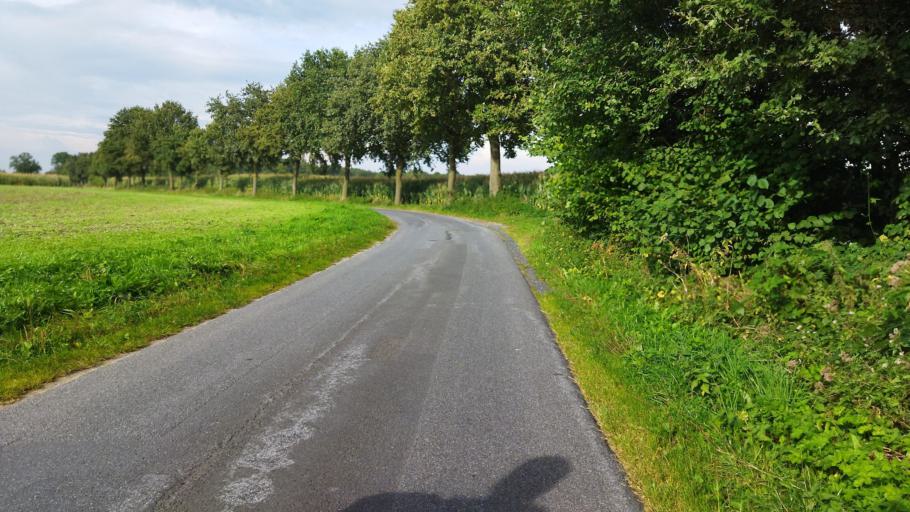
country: DE
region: North Rhine-Westphalia
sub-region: Regierungsbezirk Munster
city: Telgte
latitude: 52.0264
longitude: 7.7998
